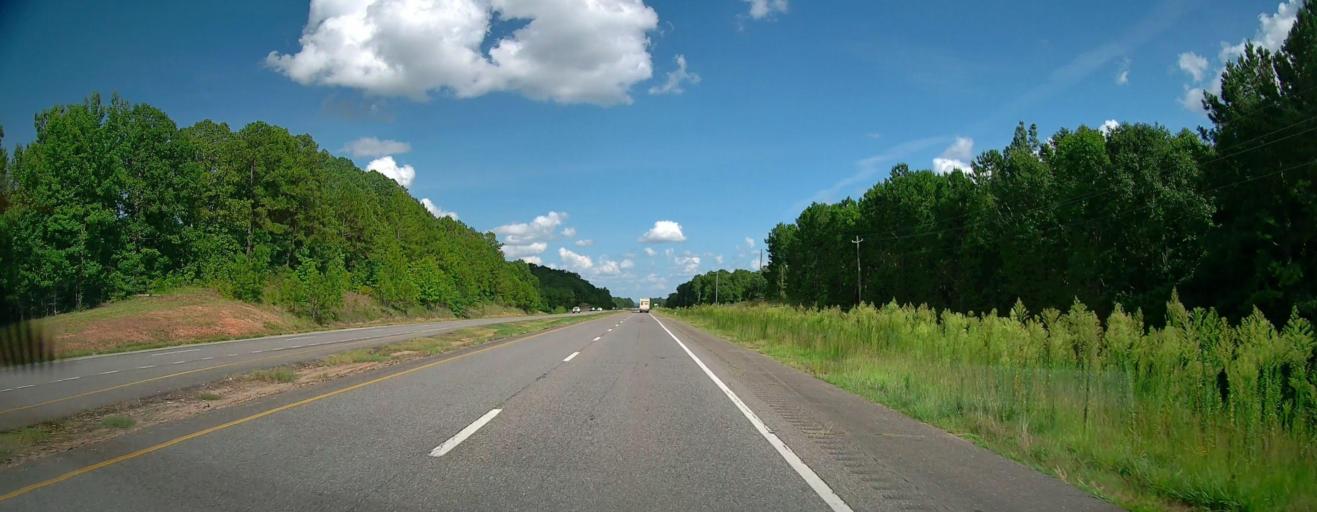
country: US
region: Alabama
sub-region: Tuscaloosa County
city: Northport
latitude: 33.2603
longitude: -87.7030
